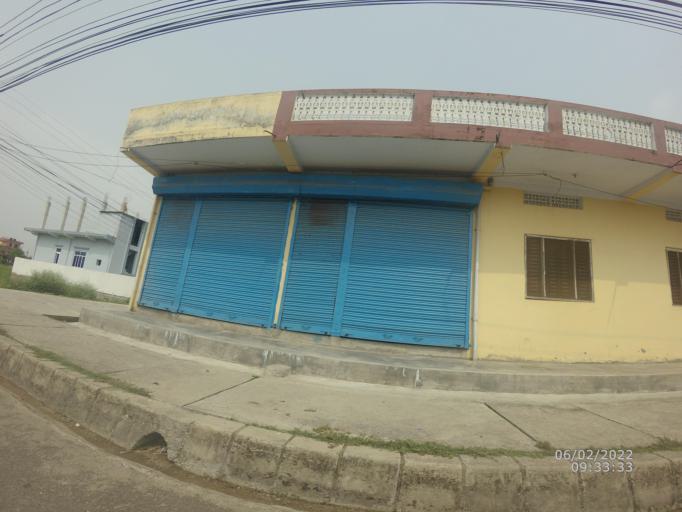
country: NP
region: Western Region
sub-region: Lumbini Zone
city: Bhairahawa
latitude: 27.4997
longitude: 83.4537
